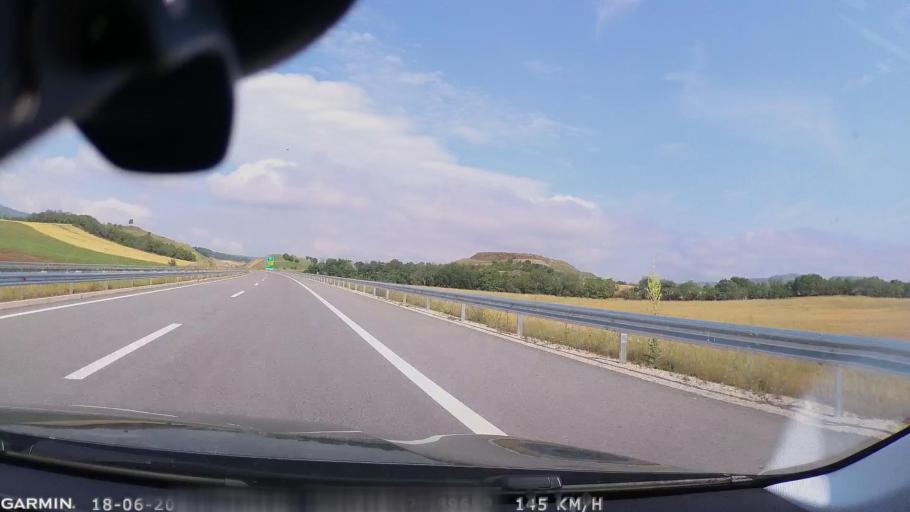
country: MK
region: Sveti Nikole
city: Gorobinci
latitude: 41.9123
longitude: 21.8957
